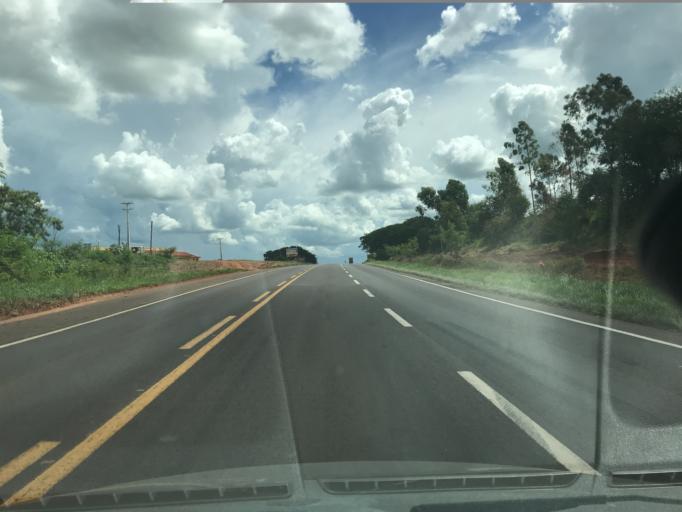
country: BR
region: Parana
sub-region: Cruzeiro Do Oeste
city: Cruzeiro do Oeste
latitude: -23.7910
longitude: -53.0378
